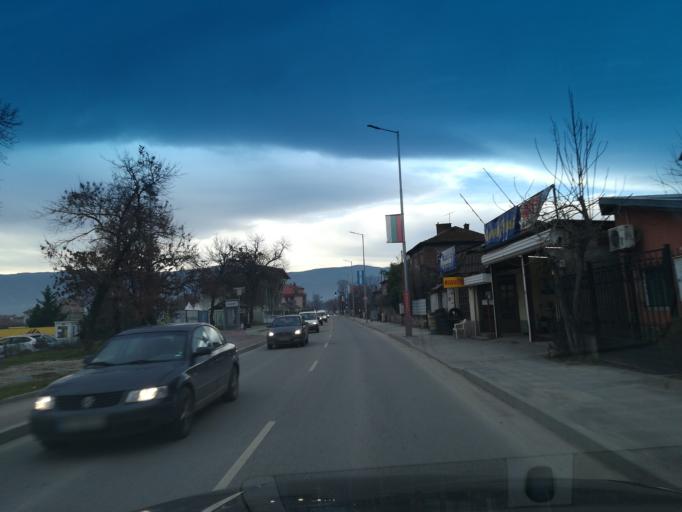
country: BG
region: Plovdiv
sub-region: Obshtina Plovdiv
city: Plovdiv
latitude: 42.1080
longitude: 24.7064
